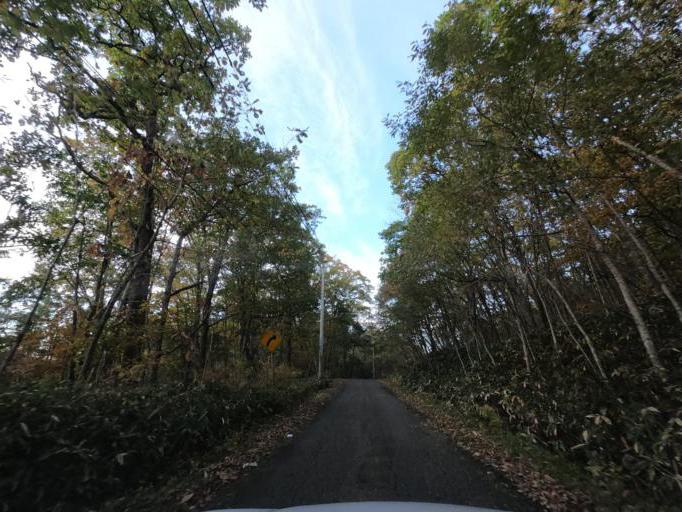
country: JP
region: Hokkaido
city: Obihiro
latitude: 42.5854
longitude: 143.3078
